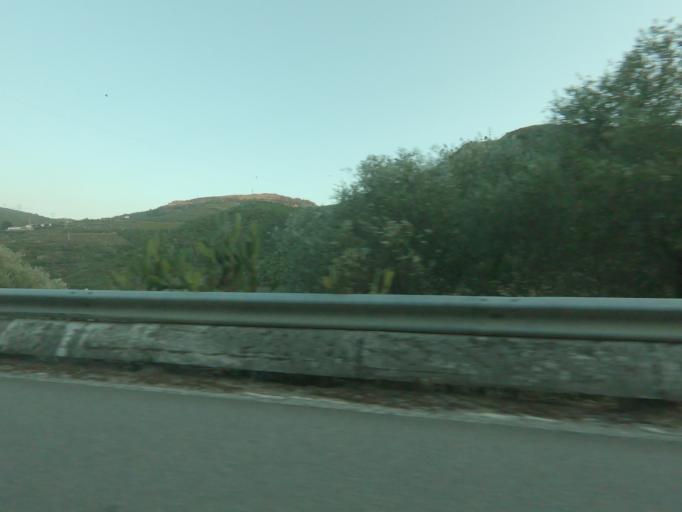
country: PT
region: Vila Real
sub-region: Peso da Regua
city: Peso da Regua
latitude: 41.1490
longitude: -7.7452
